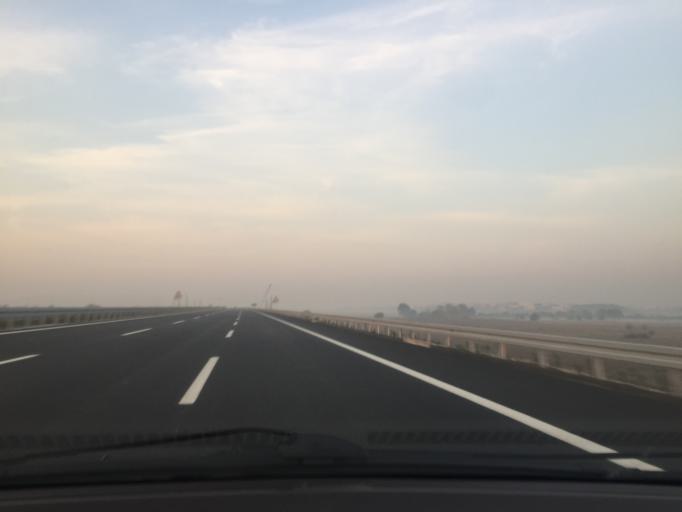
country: TR
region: Bursa
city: Karacabey
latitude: 40.2260
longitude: 28.4073
